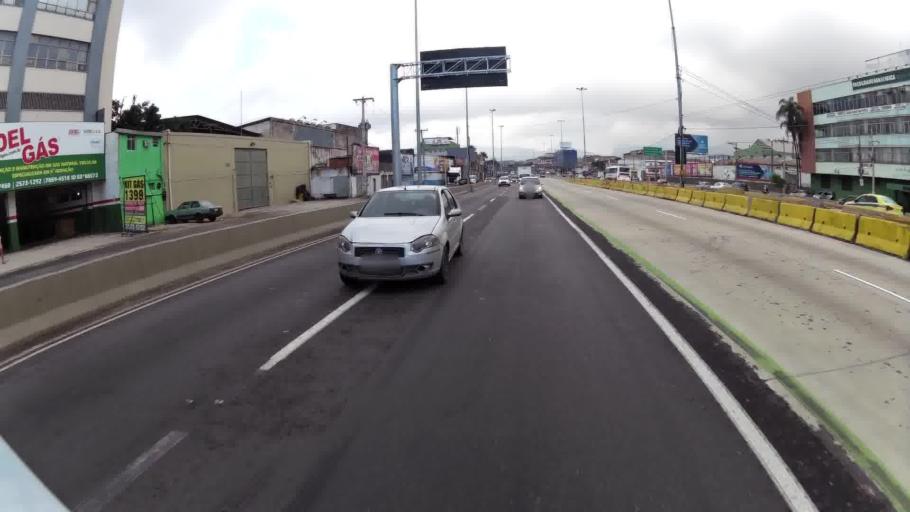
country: BR
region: Rio de Janeiro
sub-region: Rio De Janeiro
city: Rio de Janeiro
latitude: -22.8616
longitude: -43.2478
